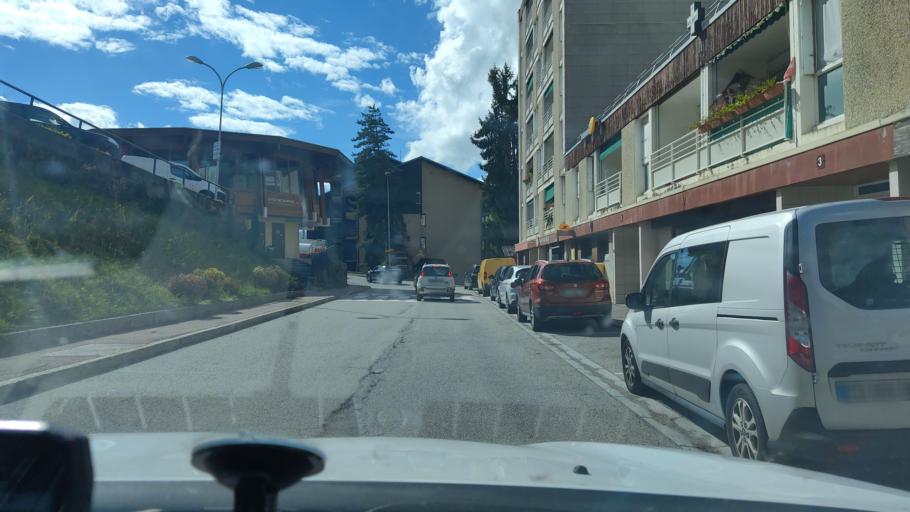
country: FR
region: Rhone-Alpes
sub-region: Departement de la Haute-Savoie
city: Praz-sur-Arly
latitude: 45.8181
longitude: 6.5138
